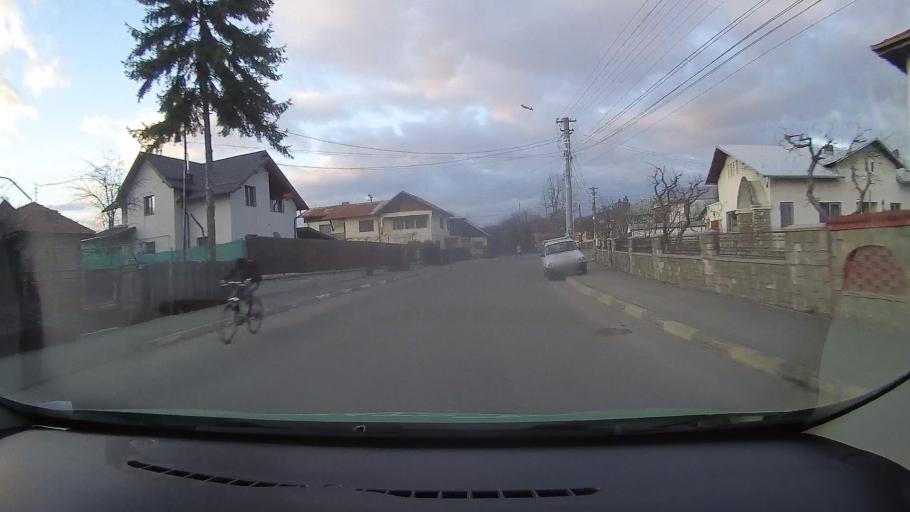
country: RO
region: Dambovita
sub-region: Municipiul Moreni
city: Moreni
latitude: 44.9937
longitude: 25.6464
